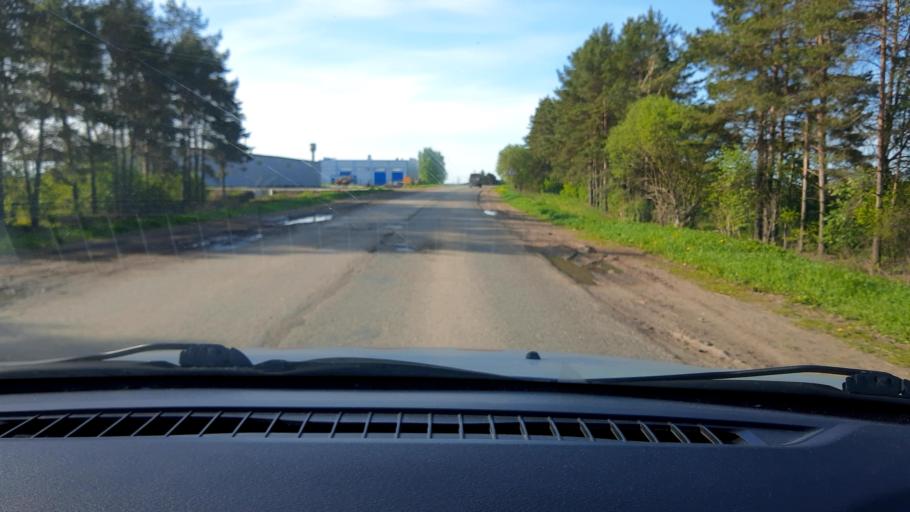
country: RU
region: Nizjnij Novgorod
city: Burevestnik
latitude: 56.1571
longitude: 43.7768
